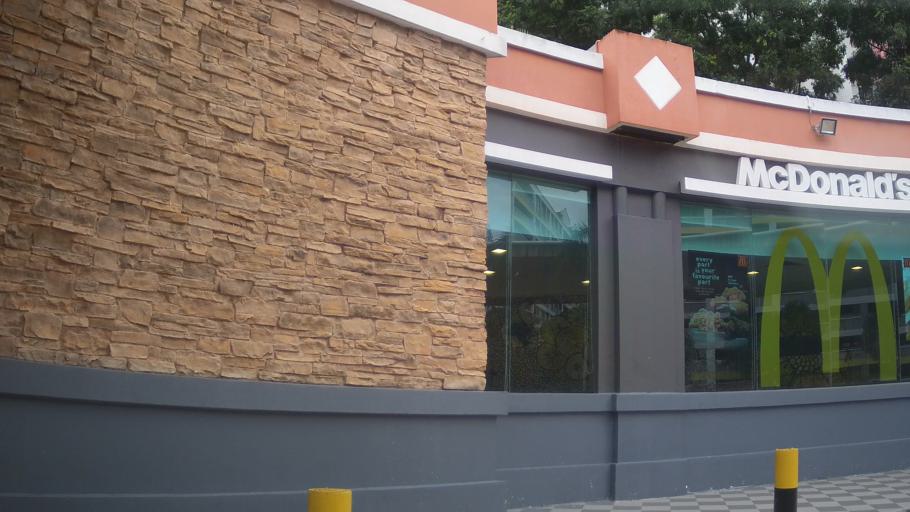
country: MY
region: Johor
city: Johor Bahru
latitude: 1.3839
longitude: 103.7704
